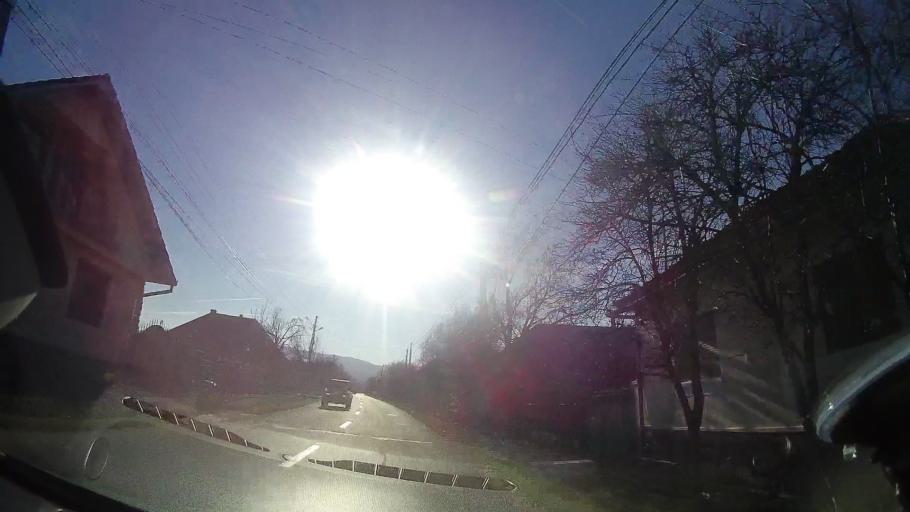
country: RO
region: Bihor
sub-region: Comuna Vadu Crisului
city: Vadu Crisului
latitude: 46.9964
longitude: 22.5223
